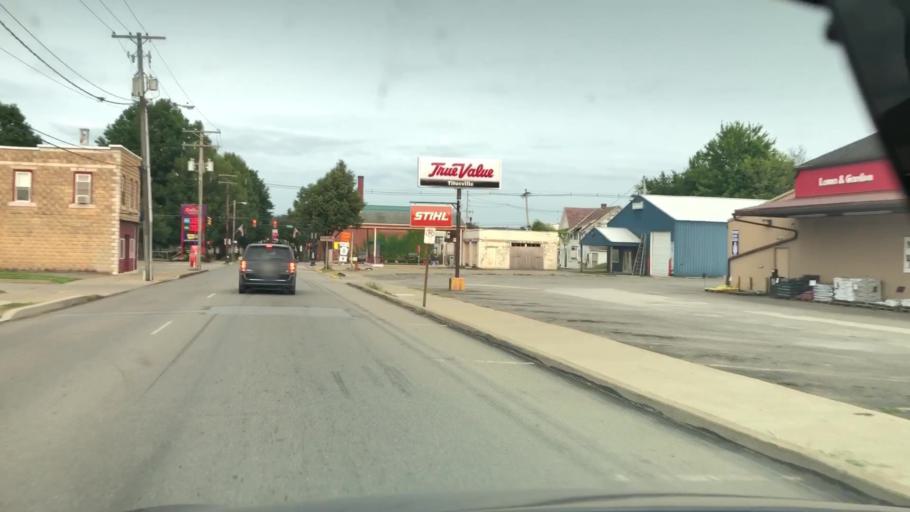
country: US
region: Pennsylvania
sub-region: Crawford County
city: Titusville
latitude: 41.6264
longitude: -79.6785
